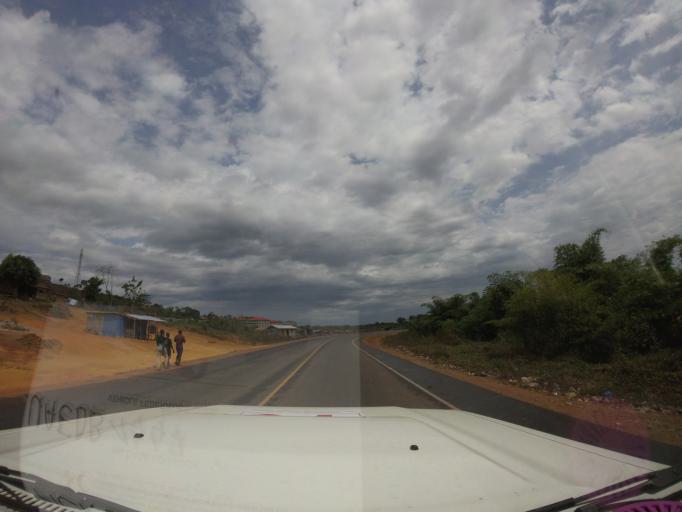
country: LR
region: Montserrado
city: Bensonville City
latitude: 6.3371
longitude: -10.6593
